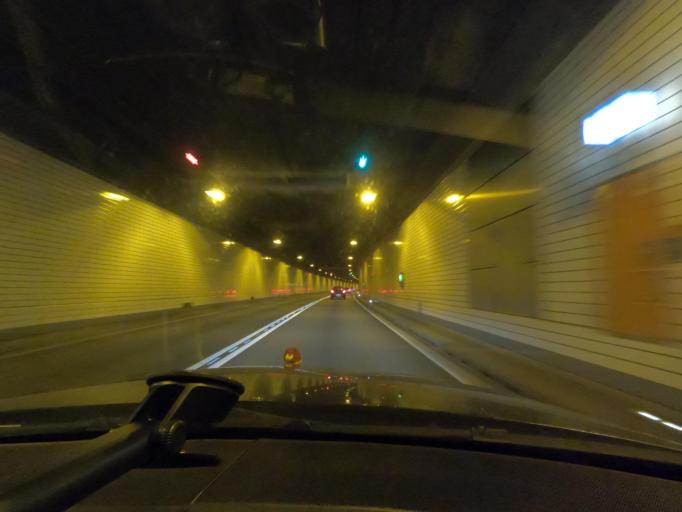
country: DE
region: Hamburg
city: Neustadt
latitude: 53.5407
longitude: 9.9809
